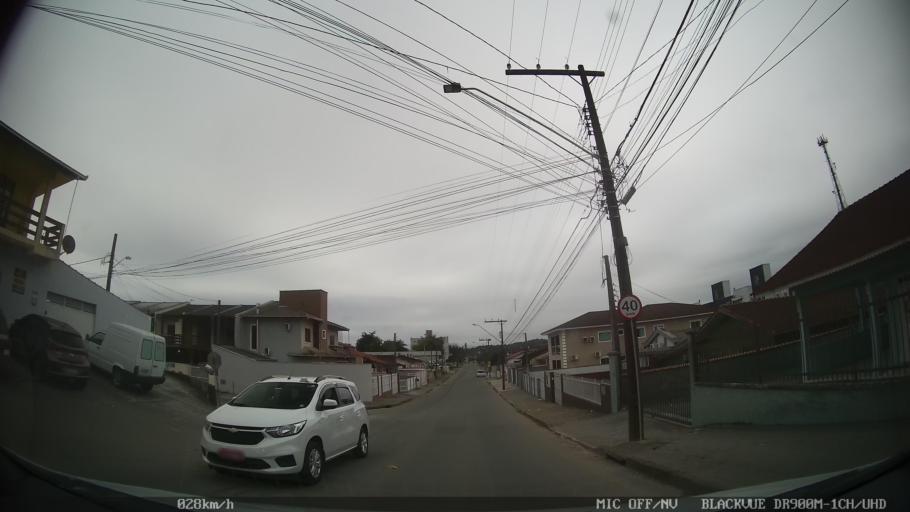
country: BR
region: Santa Catarina
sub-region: Joinville
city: Joinville
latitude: -26.2915
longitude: -48.9011
